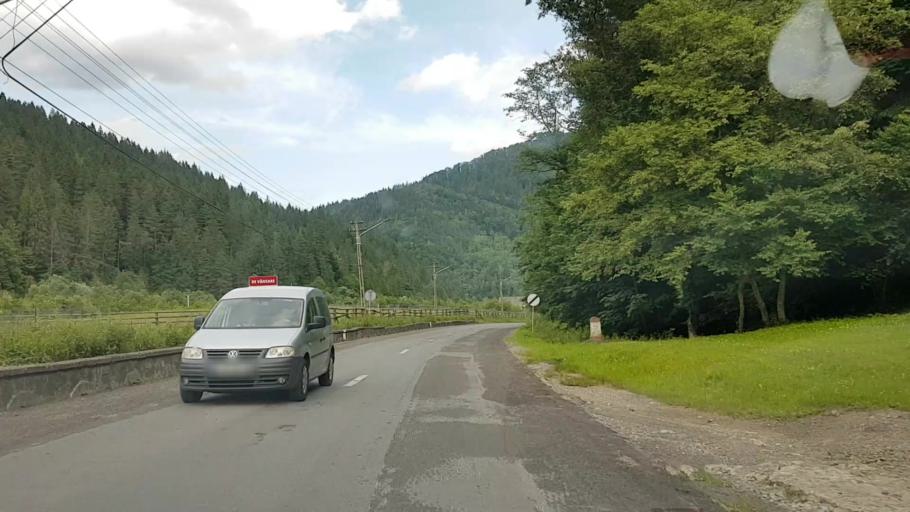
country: RO
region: Neamt
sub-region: Comuna Bicaz
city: Dodeni
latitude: 46.9380
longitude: 26.0871
